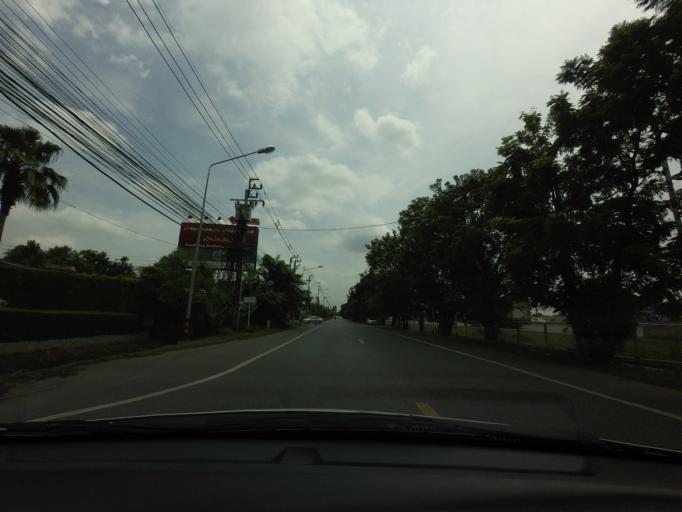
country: TH
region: Bangkok
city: Khan Na Yao
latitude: 13.8619
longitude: 100.6770
